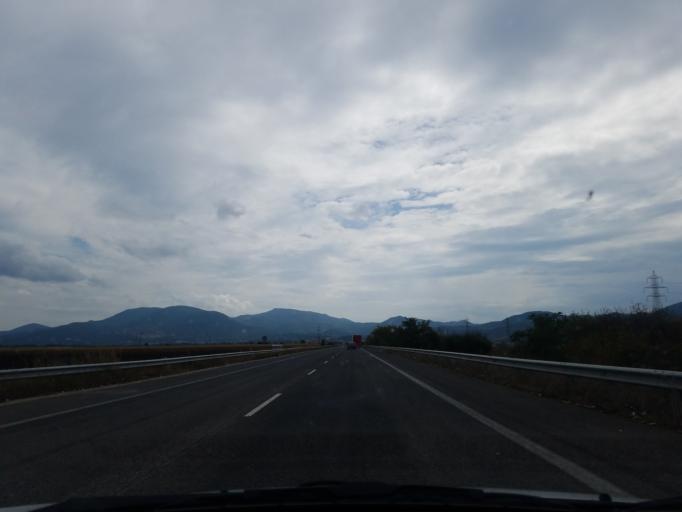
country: GR
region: Central Greece
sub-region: Nomos Fthiotidos
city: Domokos
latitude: 39.0523
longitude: 22.3416
